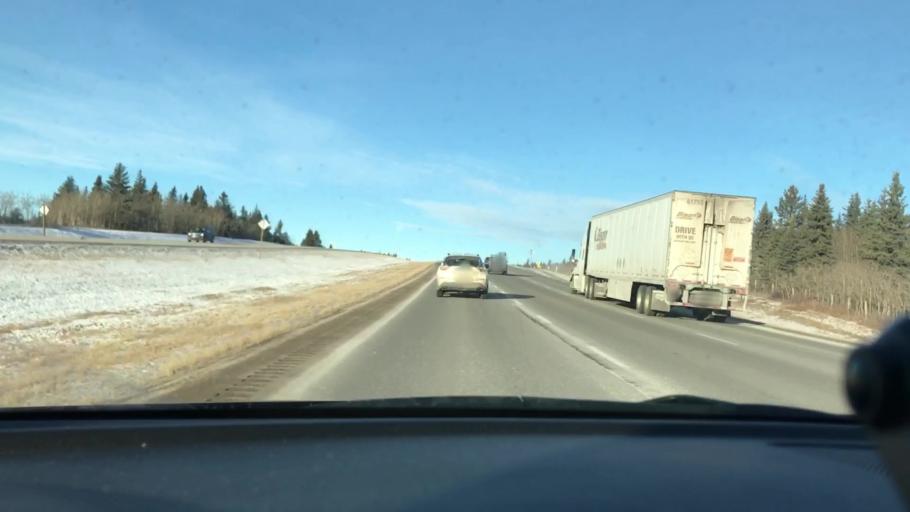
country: CA
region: Alberta
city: Cochrane
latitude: 51.1407
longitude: -114.7178
